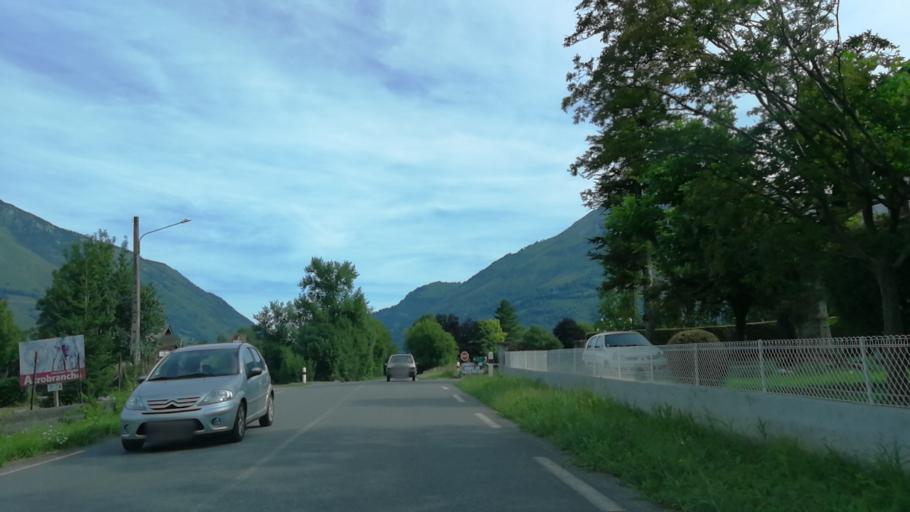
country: FR
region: Aquitaine
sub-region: Departement des Pyrenees-Atlantiques
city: Arette
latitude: 42.9743
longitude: -0.6075
